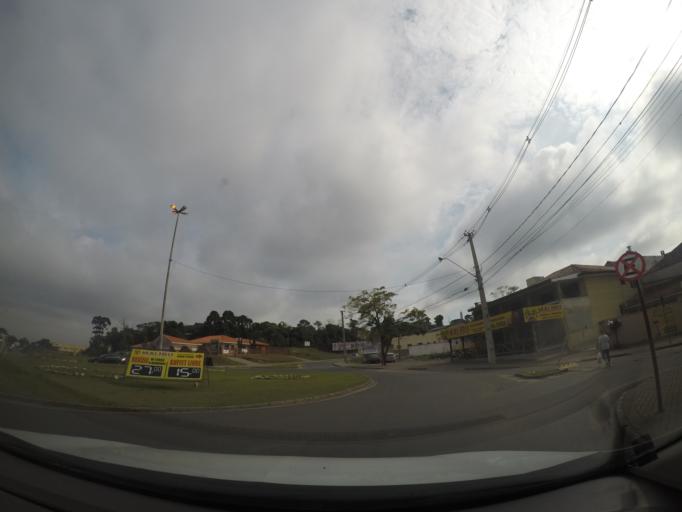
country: BR
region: Parana
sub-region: Colombo
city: Colombo
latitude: -25.3502
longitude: -49.2016
